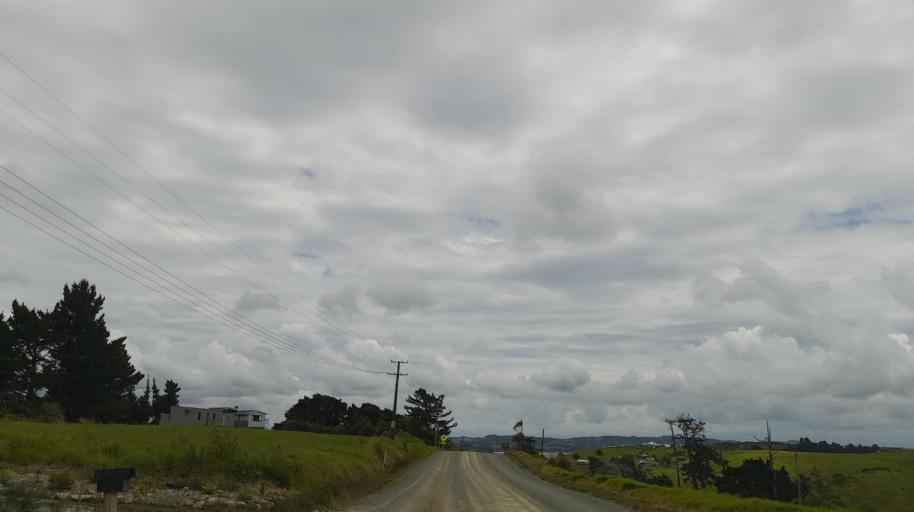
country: NZ
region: Auckland
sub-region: Auckland
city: Wellsford
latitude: -36.2678
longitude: 174.4090
